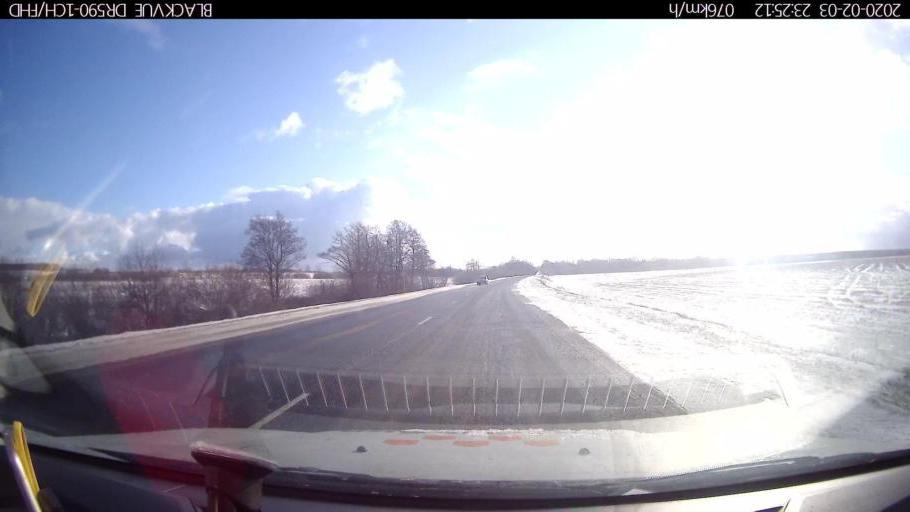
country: RU
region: Nizjnij Novgorod
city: Kstovo
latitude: 56.0069
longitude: 44.2095
